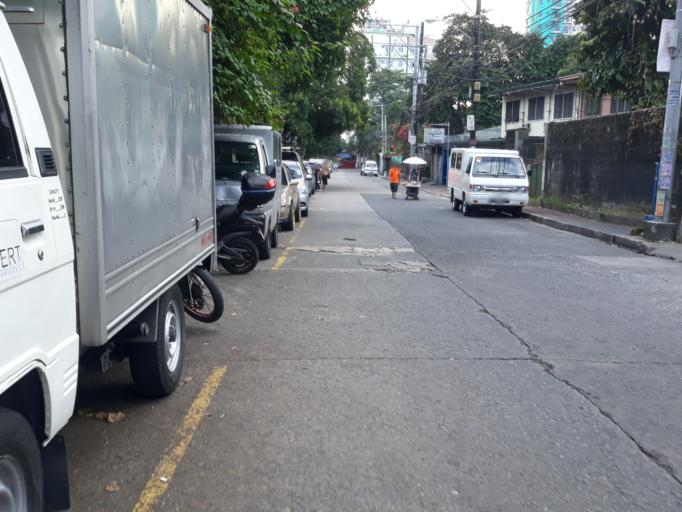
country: PH
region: Metro Manila
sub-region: San Juan
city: San Juan
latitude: 14.6183
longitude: 121.0465
